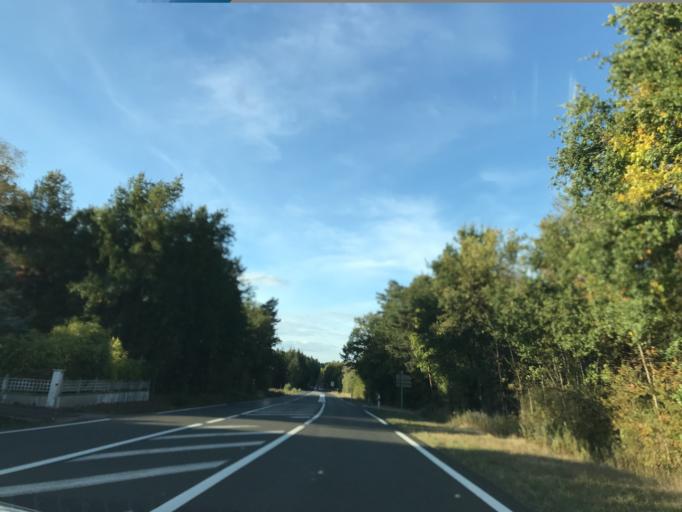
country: FR
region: Auvergne
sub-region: Departement du Puy-de-Dome
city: Paslieres
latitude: 45.9123
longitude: 3.5153
